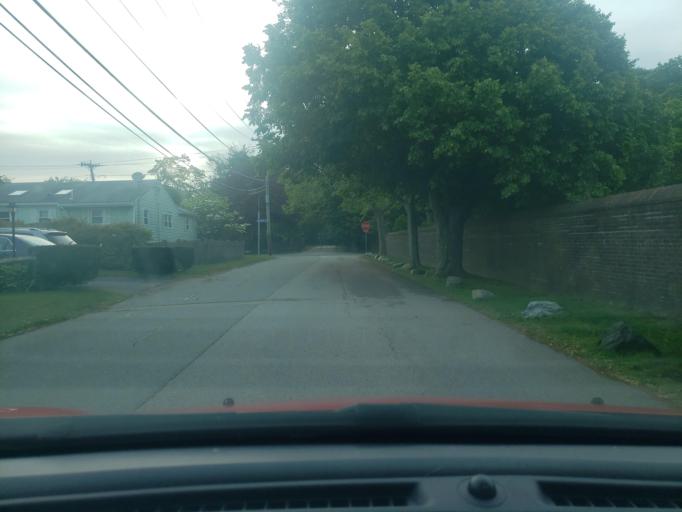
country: US
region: Rhode Island
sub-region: Newport County
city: Newport
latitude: 41.4781
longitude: -71.3027
